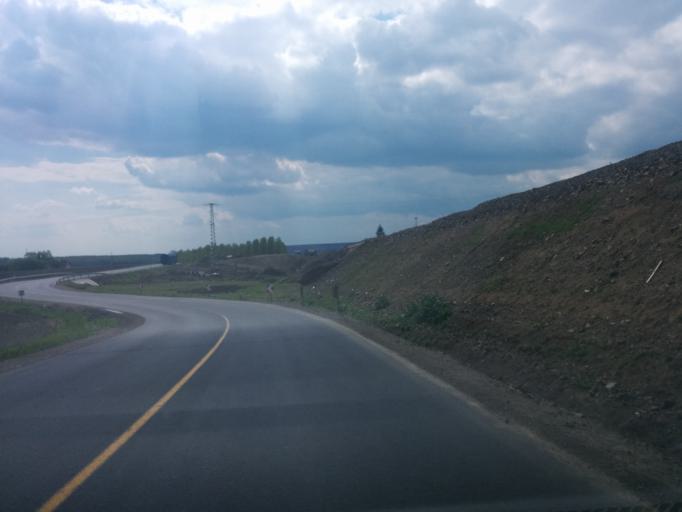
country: HU
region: Nograd
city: Paszto
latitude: 47.9466
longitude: 19.7057
